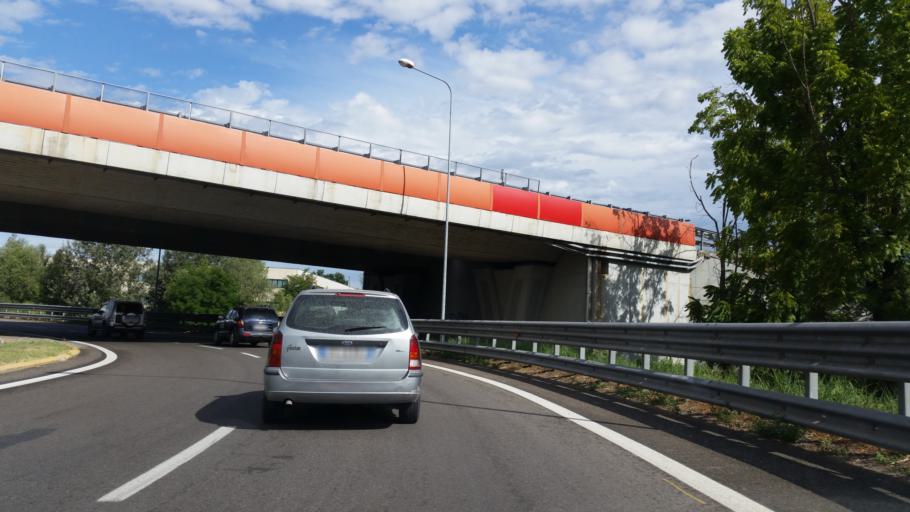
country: IT
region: Piedmont
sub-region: Provincia di Cuneo
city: Sant'Antonio
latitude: 44.7438
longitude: 8.0737
